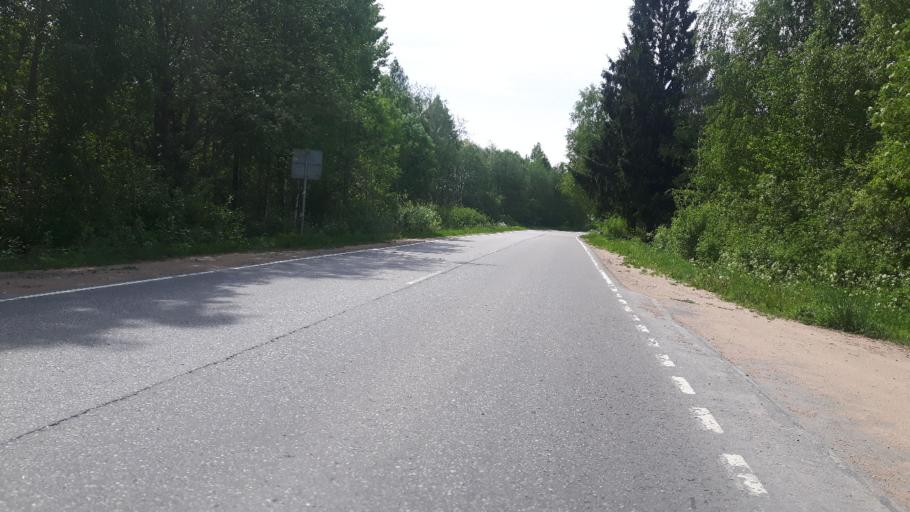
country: RU
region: Leningrad
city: Ust'-Luga
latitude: 59.6515
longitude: 28.2381
